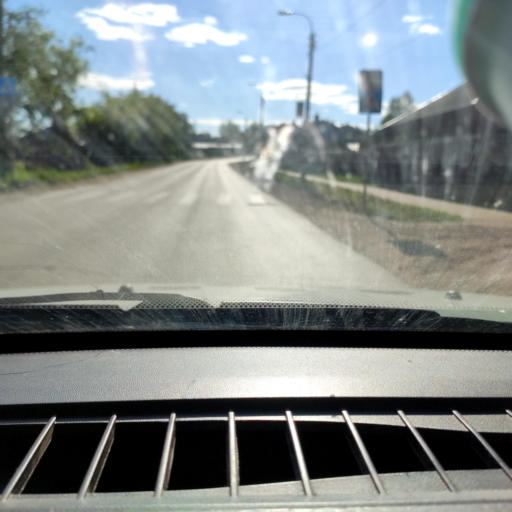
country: RU
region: Perm
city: Ocher
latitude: 57.8819
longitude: 54.7217
